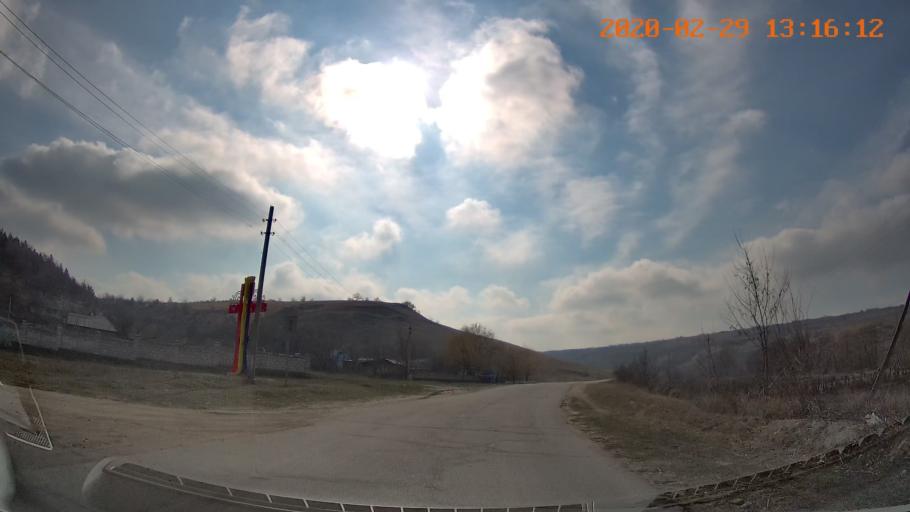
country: MD
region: Telenesti
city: Camenca
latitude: 48.0042
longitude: 28.6662
